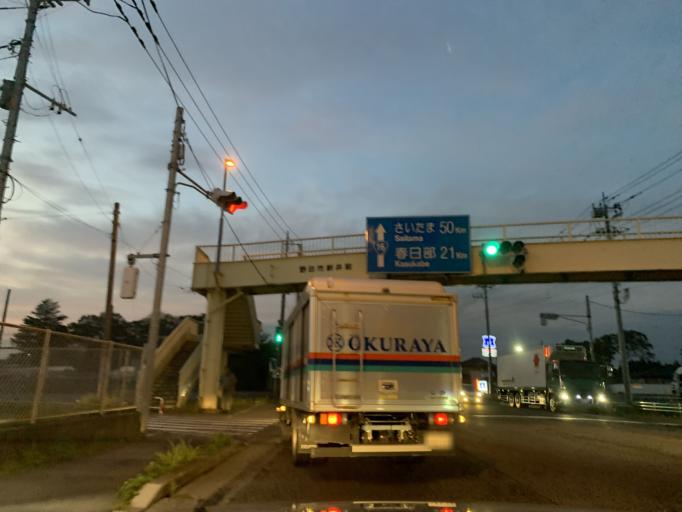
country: JP
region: Chiba
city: Nagareyama
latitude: 35.9190
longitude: 139.9250
